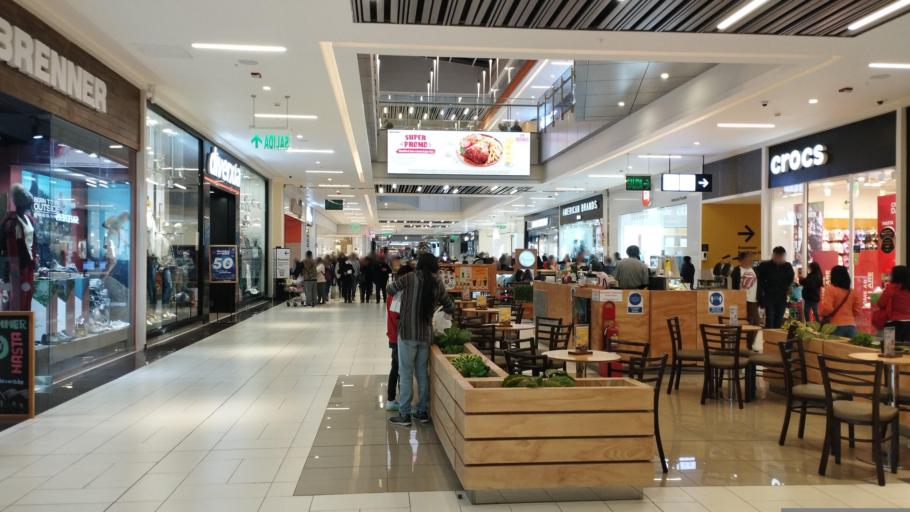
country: PE
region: Cusco
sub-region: Provincia de Cusco
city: Cusco
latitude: -13.5250
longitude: -71.9505
